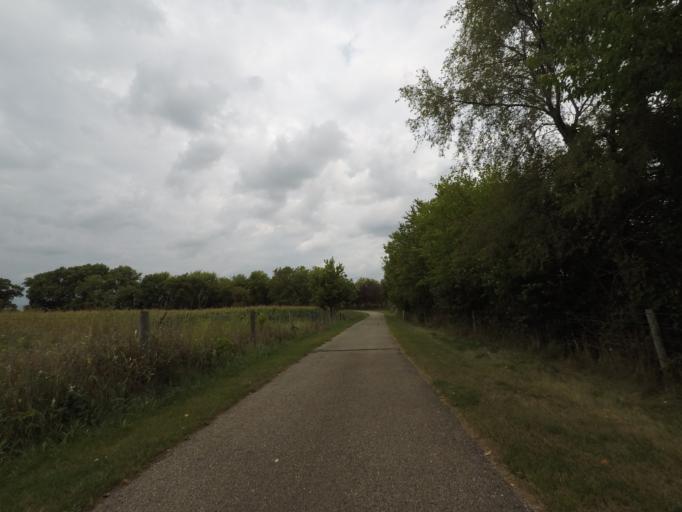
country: US
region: Wisconsin
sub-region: Jefferson County
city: Lake Koshkonong
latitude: 42.8880
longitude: -88.8726
